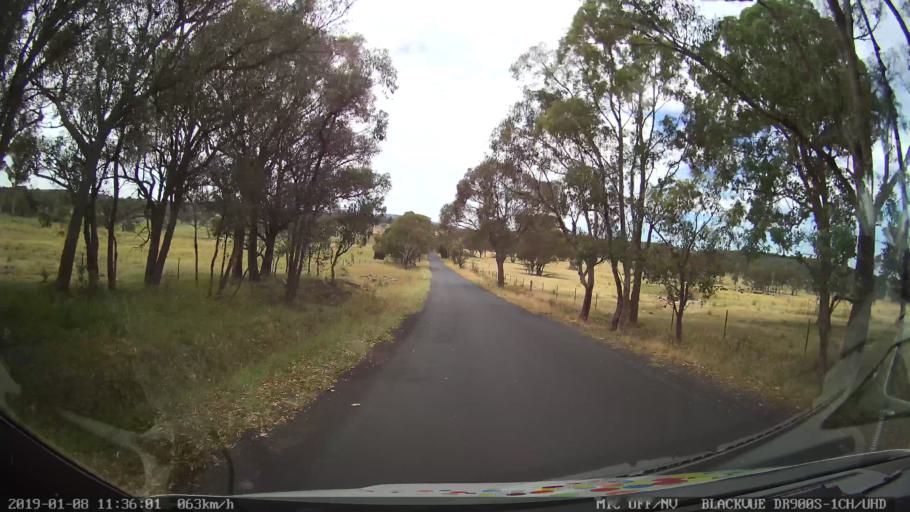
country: AU
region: New South Wales
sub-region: Guyra
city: Guyra
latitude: -30.3426
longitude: 151.5401
